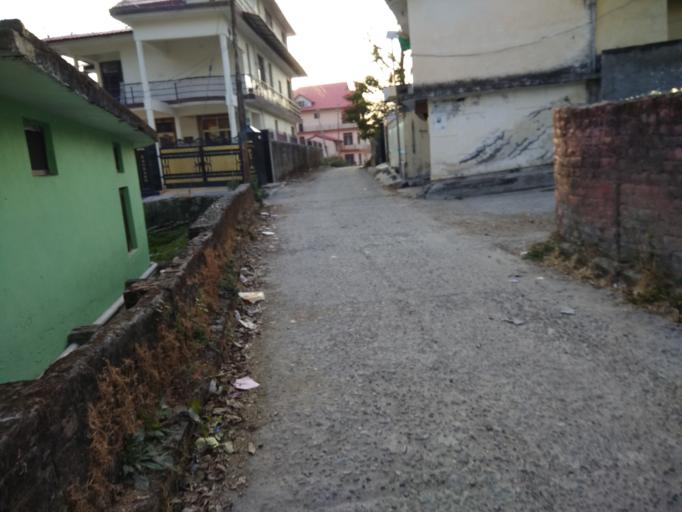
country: IN
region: Himachal Pradesh
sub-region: Kangra
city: Palampur
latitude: 32.1174
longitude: 76.5298
